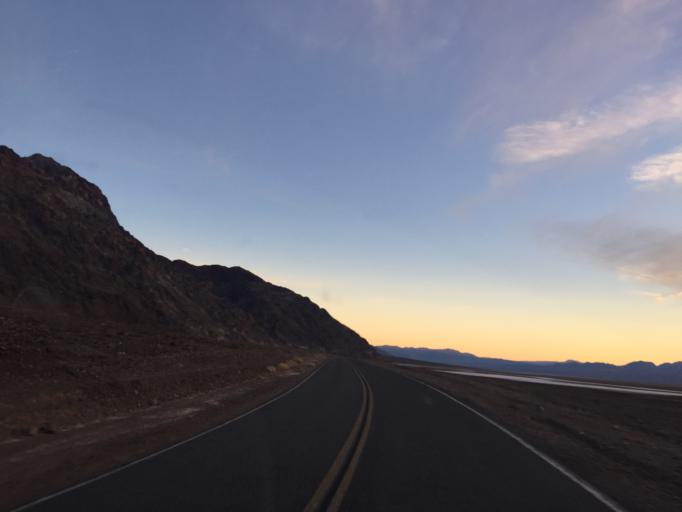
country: US
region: Nevada
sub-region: Nye County
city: Beatty
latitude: 36.1948
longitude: -116.7725
